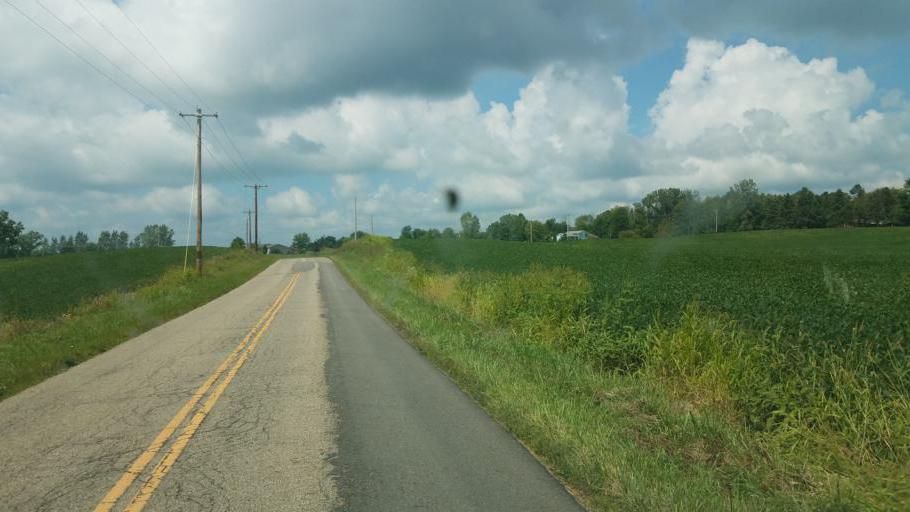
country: US
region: Ohio
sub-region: Knox County
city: Mount Vernon
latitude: 40.3152
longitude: -82.4905
